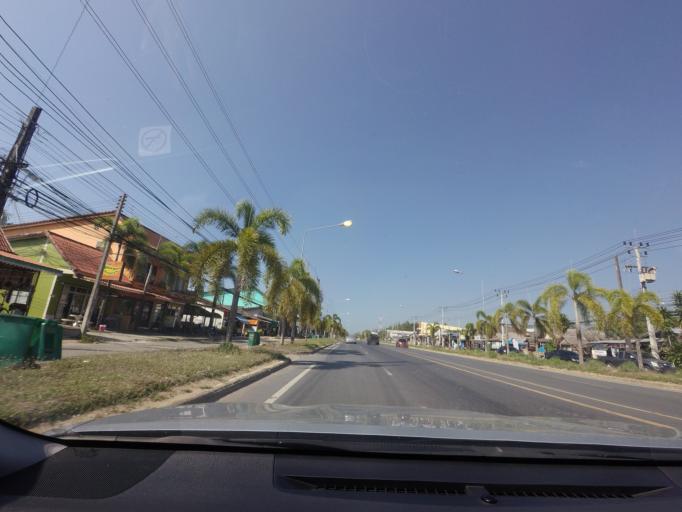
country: TH
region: Phangnga
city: Ban Khao Lak
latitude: 8.6688
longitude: 98.2530
